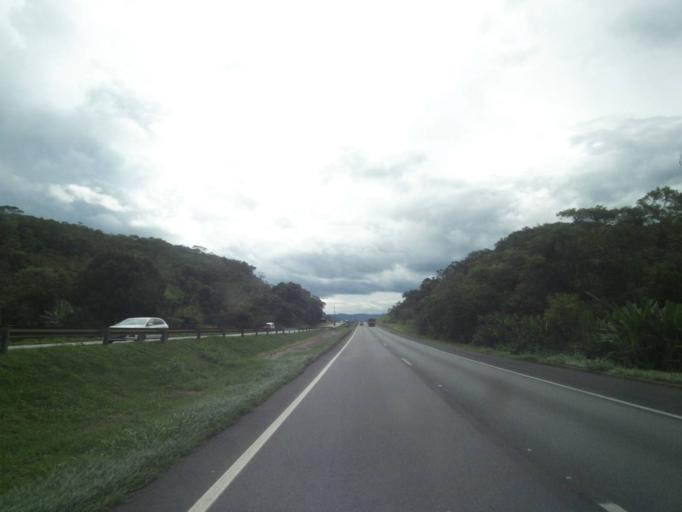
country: BR
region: Parana
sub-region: Antonina
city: Antonina
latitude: -25.5321
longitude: -48.7530
